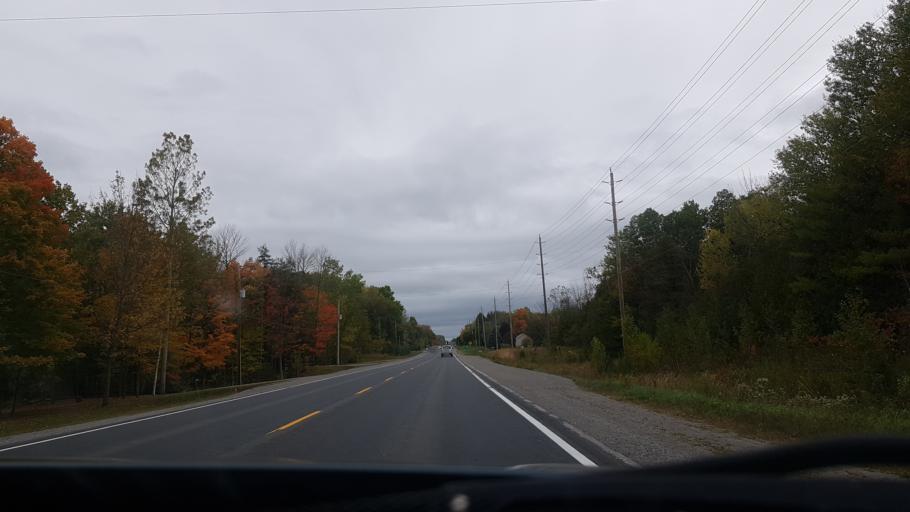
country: CA
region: Ontario
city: Omemee
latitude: 44.1973
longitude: -78.4785
